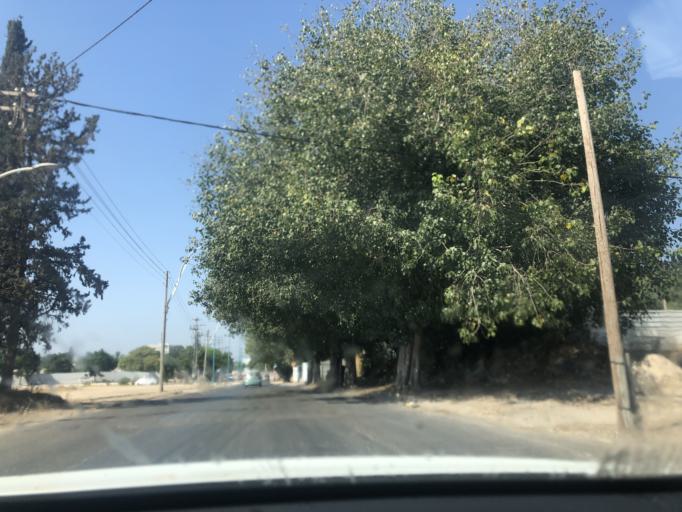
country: IL
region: Central District
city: Lod
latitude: 31.9581
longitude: 34.8979
